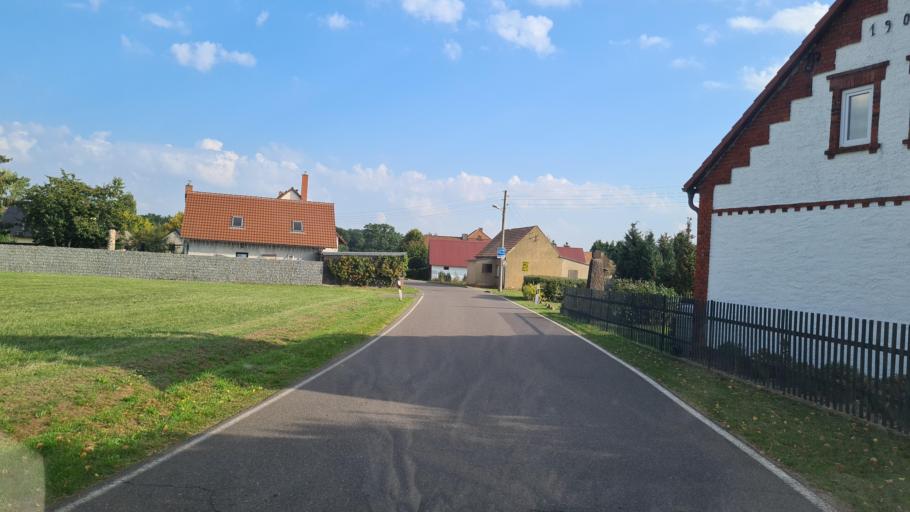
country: DE
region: Brandenburg
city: Neupetershain
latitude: 51.6499
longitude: 14.1756
